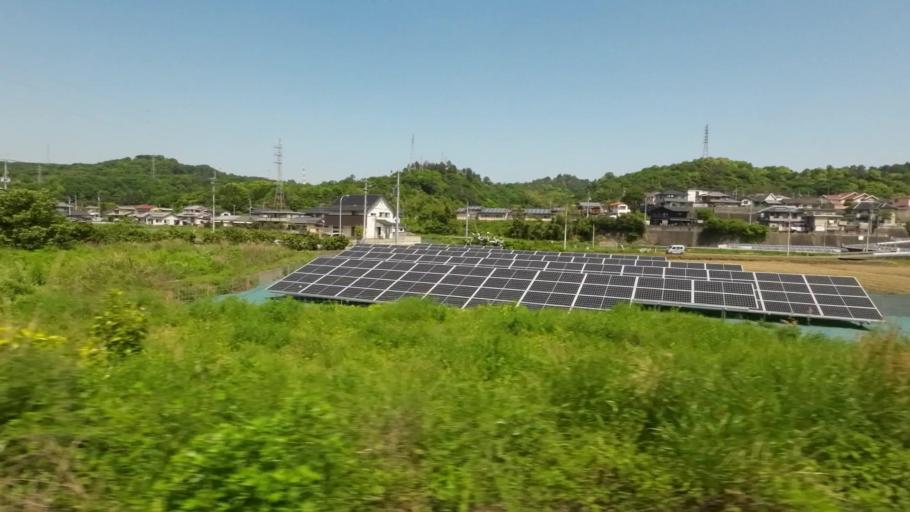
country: JP
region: Ehime
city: Niihama
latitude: 33.9291
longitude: 133.2683
